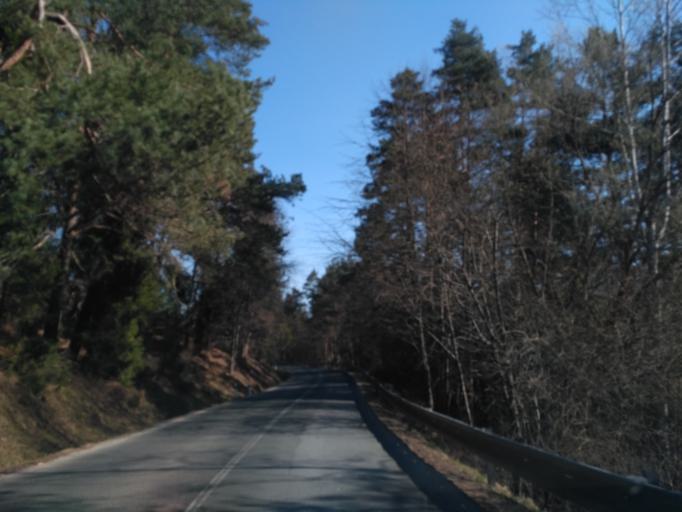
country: SK
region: Kosicky
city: Medzev
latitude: 48.7894
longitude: 20.8026
